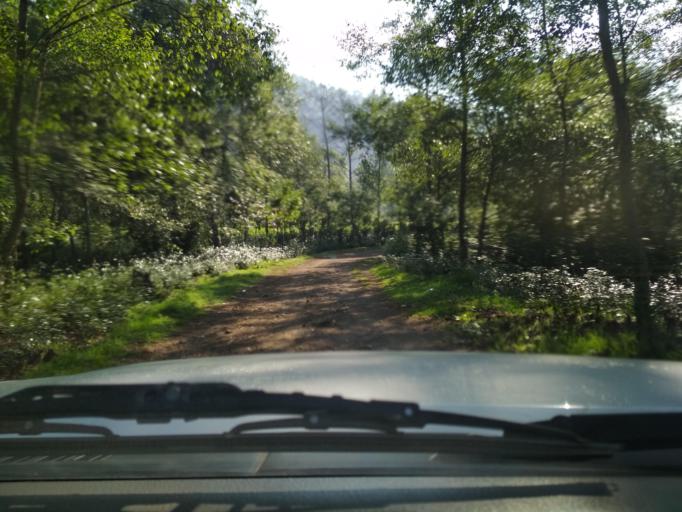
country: MX
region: Veracruz
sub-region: La Perla
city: Chilapa
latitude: 18.9853
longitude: -97.1667
